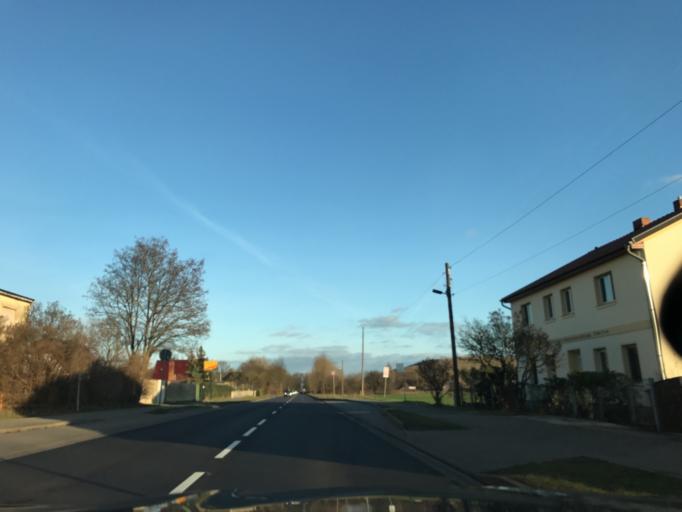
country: DE
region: Saxony-Anhalt
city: Burg bei Magdeburg
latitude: 52.2747
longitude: 11.8846
